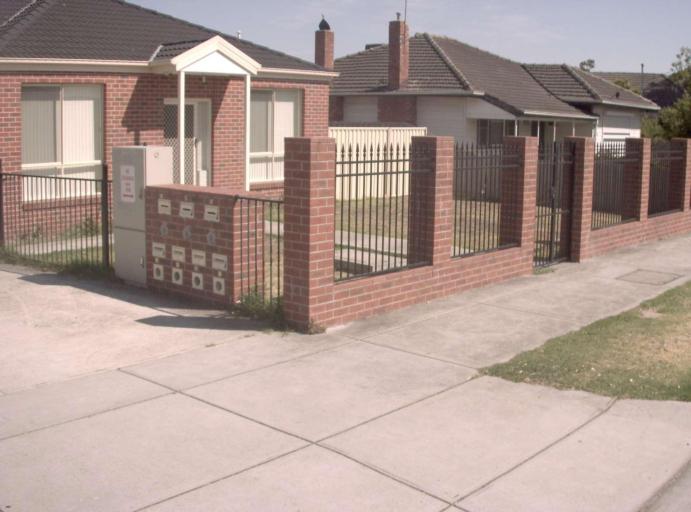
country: AU
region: Victoria
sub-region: Greater Dandenong
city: Noble Park North
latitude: -37.9625
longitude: 145.1880
